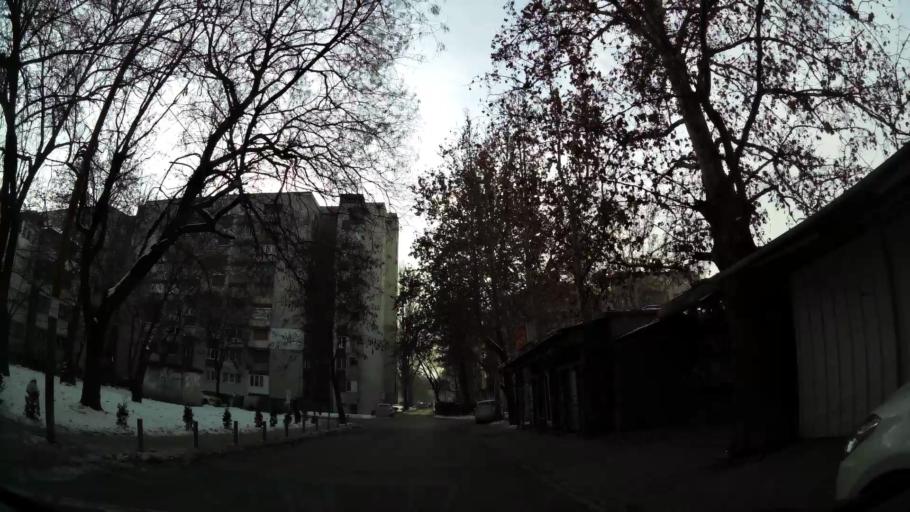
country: MK
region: Cair
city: Cair
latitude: 42.0179
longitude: 21.4326
